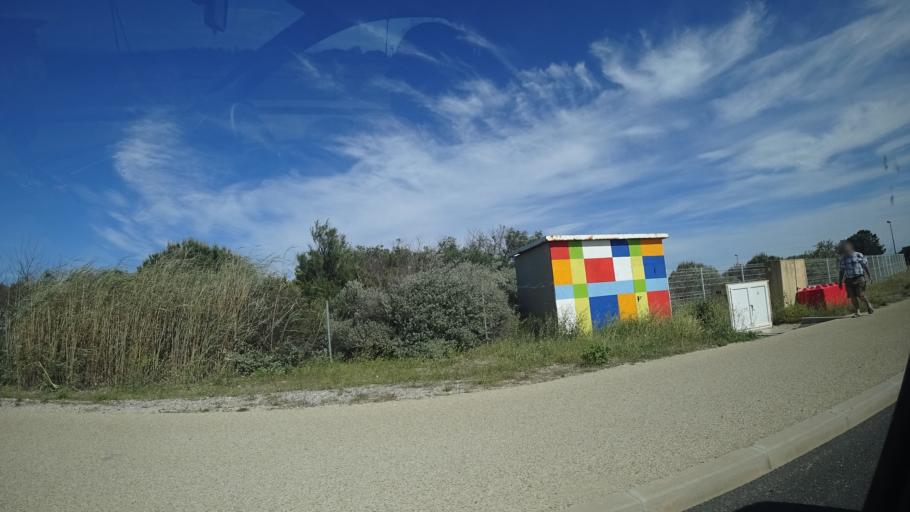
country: FR
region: Languedoc-Roussillon
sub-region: Departement des Pyrenees-Orientales
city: Le Barcares
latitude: 42.8224
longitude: 3.0347
